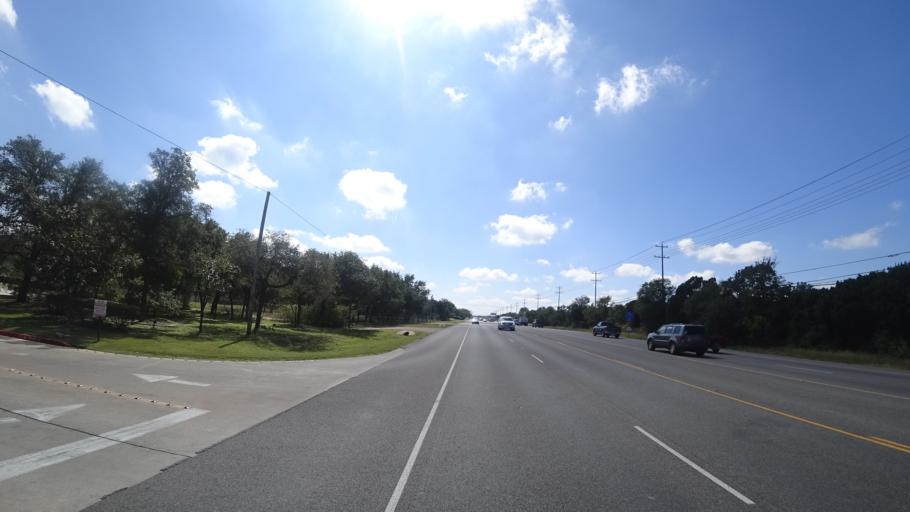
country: US
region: Texas
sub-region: Williamson County
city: Anderson Mill
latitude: 30.4108
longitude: -97.8503
